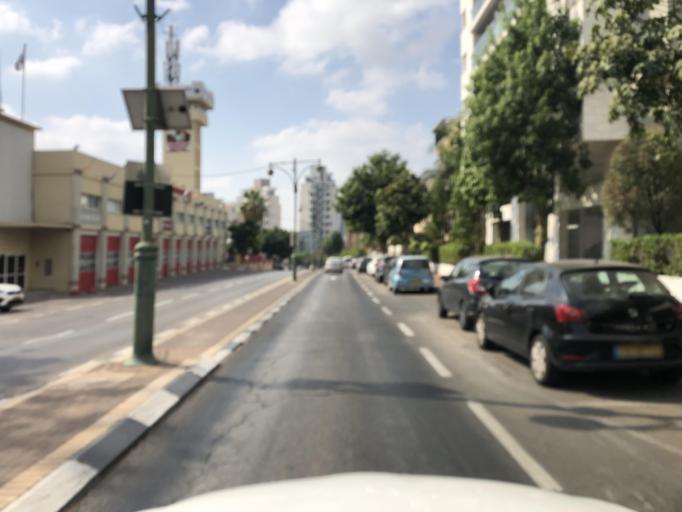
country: IL
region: Tel Aviv
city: Bene Beraq
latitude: 32.0682
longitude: 34.8326
